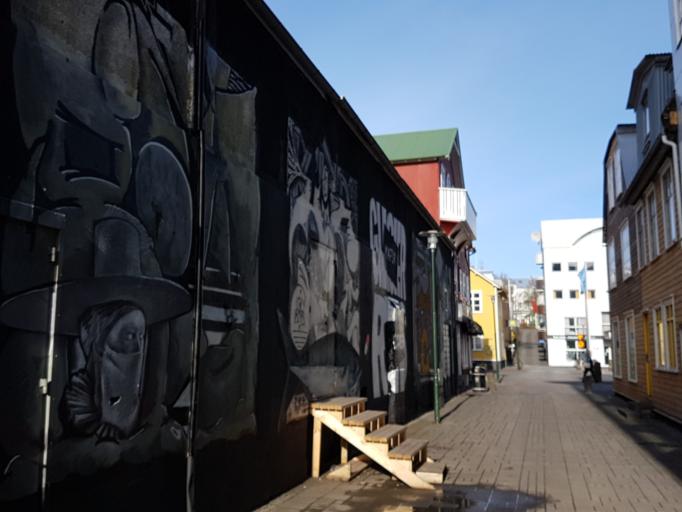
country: IS
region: Capital Region
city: Kopavogur
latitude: 64.1476
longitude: -21.9405
